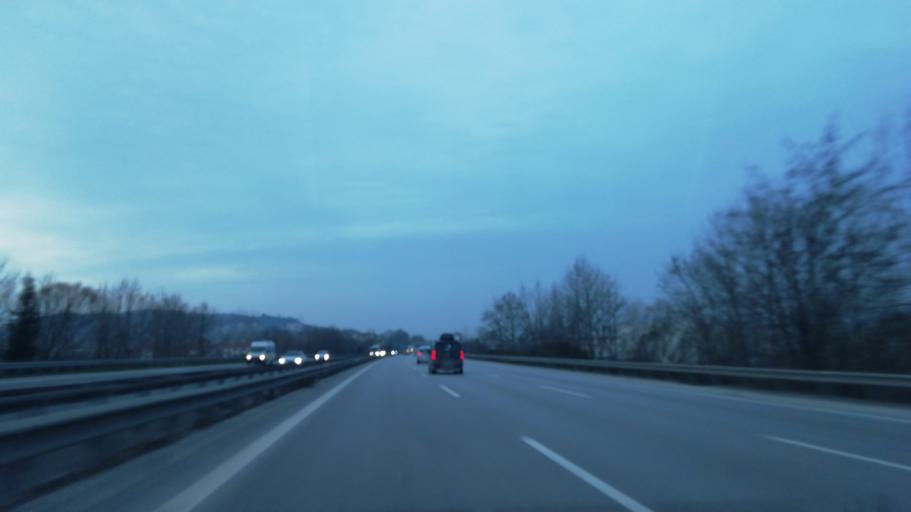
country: TR
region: Sakarya
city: Adapazari
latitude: 40.7080
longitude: 30.3661
